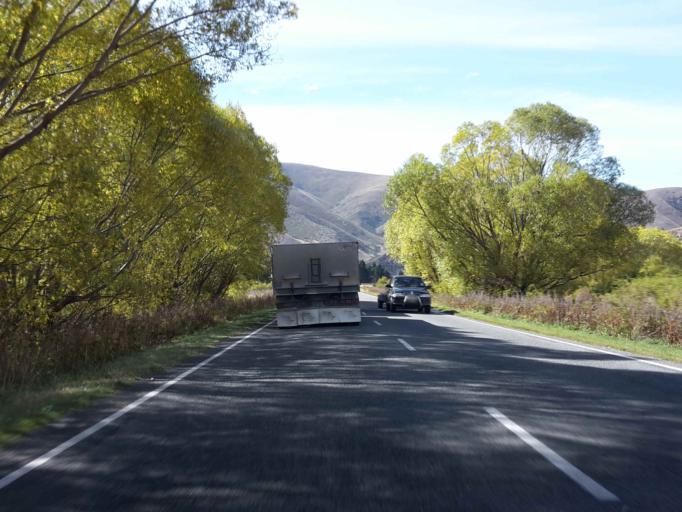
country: NZ
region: Otago
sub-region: Queenstown-Lakes District
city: Wanaka
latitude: -44.5053
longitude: 169.7447
